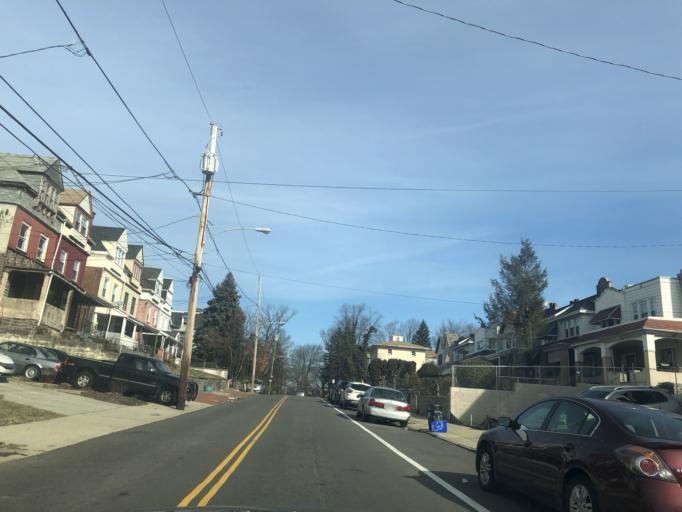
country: US
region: Pennsylvania
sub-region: Montgomery County
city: Wyndmoor
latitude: 40.0425
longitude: -75.1763
